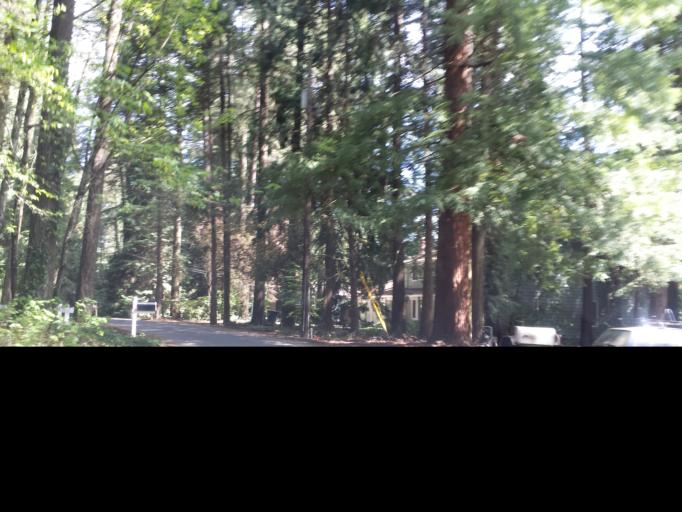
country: US
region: Oregon
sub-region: Washington County
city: Aloha
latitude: 45.5022
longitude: -122.8595
